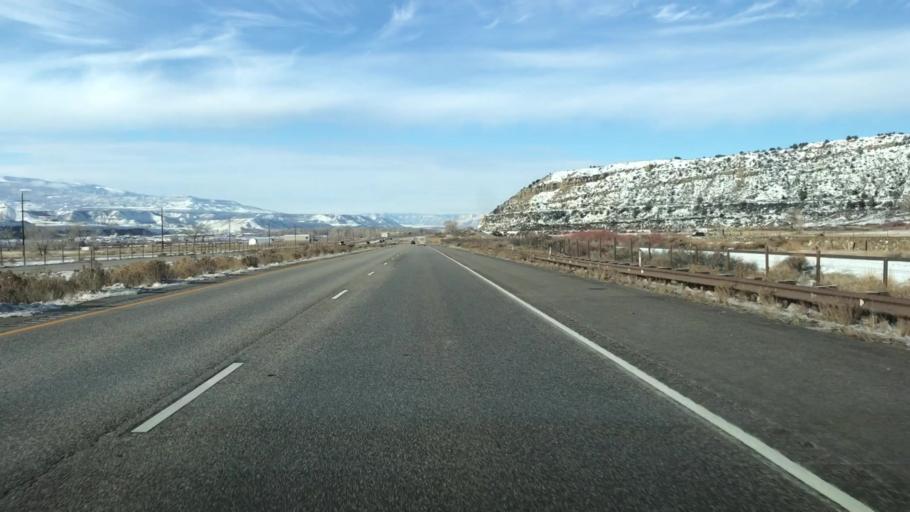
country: US
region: Colorado
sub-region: Garfield County
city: Silt
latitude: 39.5478
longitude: -107.6152
